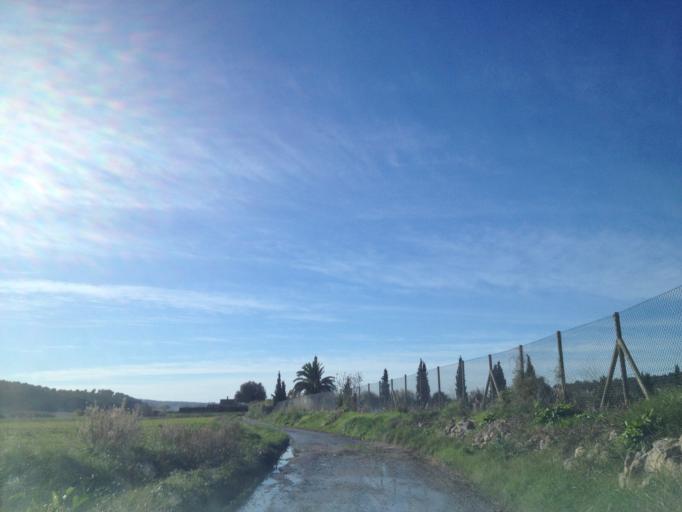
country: ES
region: Balearic Islands
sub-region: Illes Balears
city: Sineu
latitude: 39.6496
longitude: 3.0366
